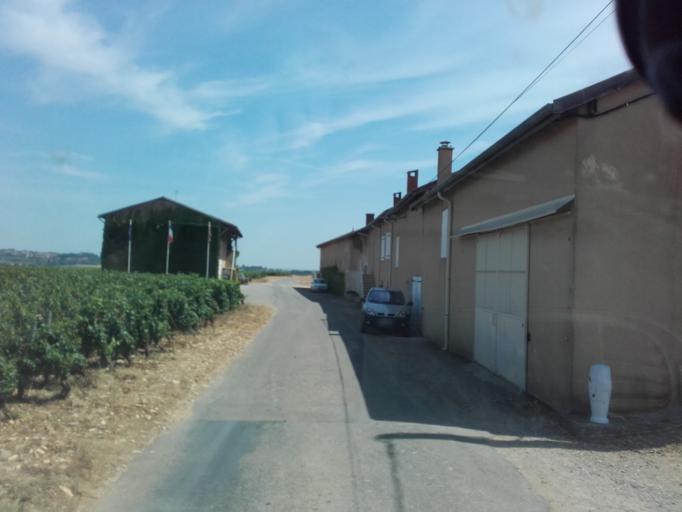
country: FR
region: Bourgogne
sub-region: Departement de Saone-et-Loire
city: Prisse
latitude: 46.2897
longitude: 4.7498
